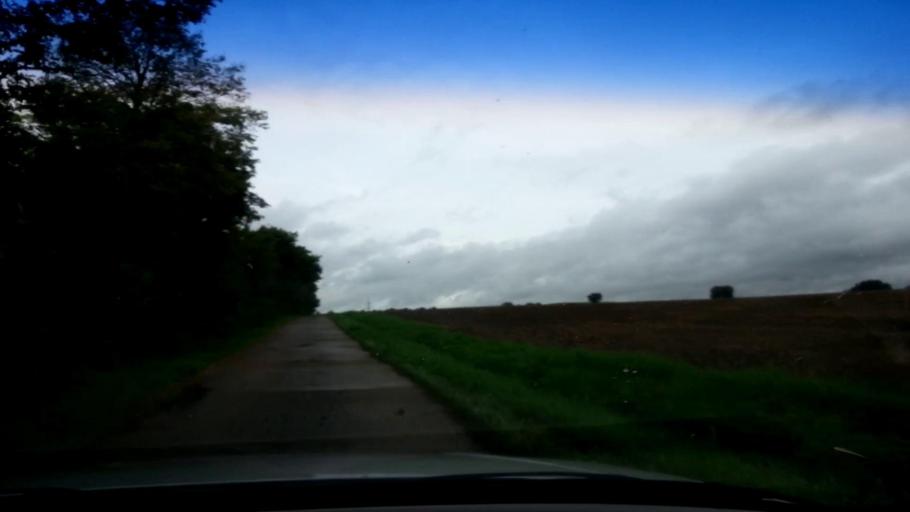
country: DE
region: Bavaria
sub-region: Upper Franconia
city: Memmelsdorf
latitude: 49.9484
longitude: 10.9810
